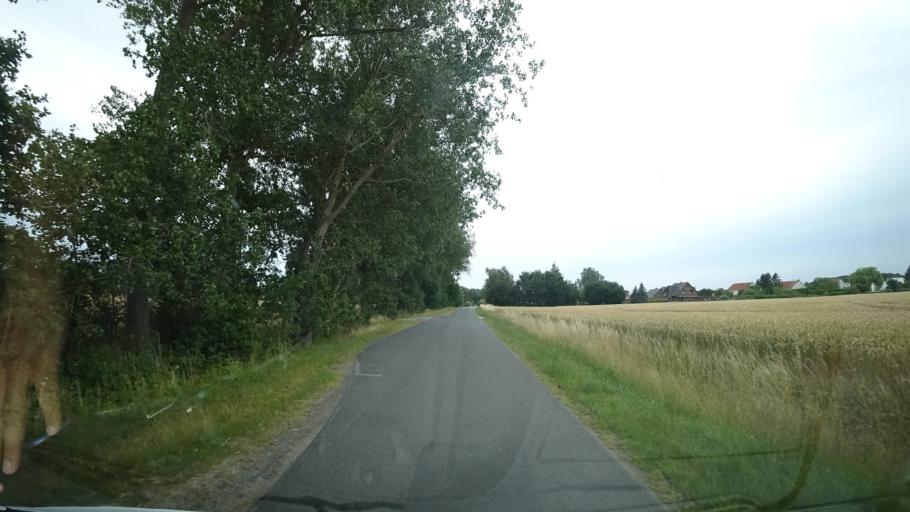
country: DE
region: Mecklenburg-Vorpommern
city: Rambin
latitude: 54.3080
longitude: 13.2113
